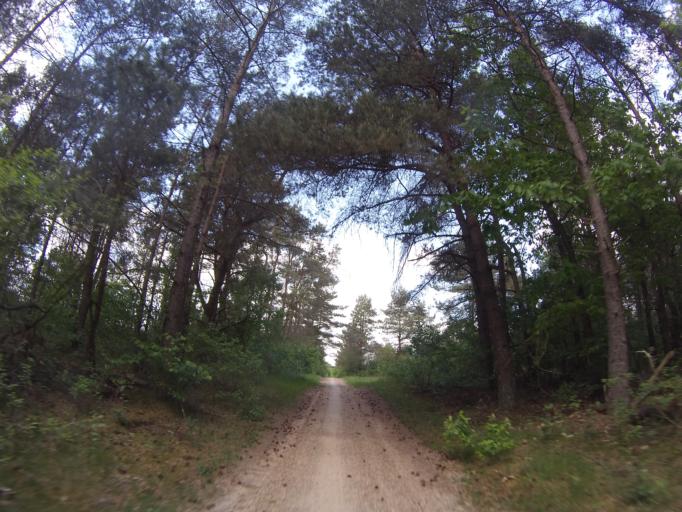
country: NL
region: Gelderland
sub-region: Gemeente Barneveld
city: Stroe
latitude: 52.1739
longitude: 5.7141
